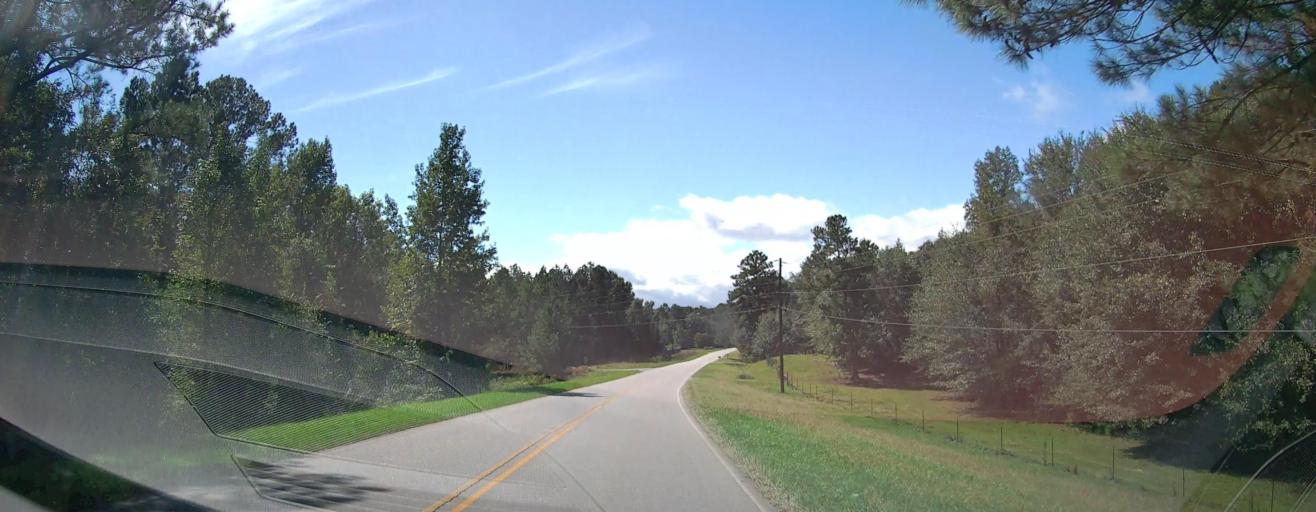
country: US
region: Georgia
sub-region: Houston County
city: Warner Robins
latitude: 32.7171
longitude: -83.5345
